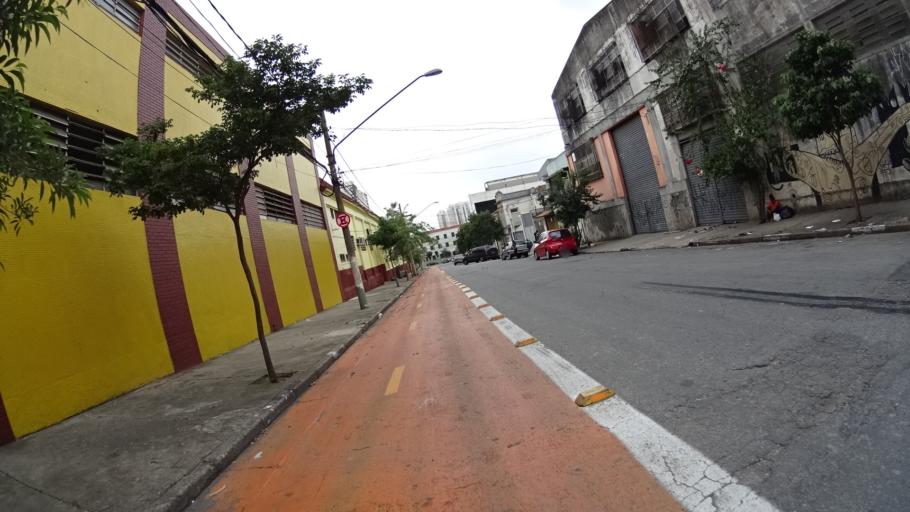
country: BR
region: Sao Paulo
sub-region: Sao Paulo
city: Sao Paulo
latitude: -23.5276
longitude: -46.6449
